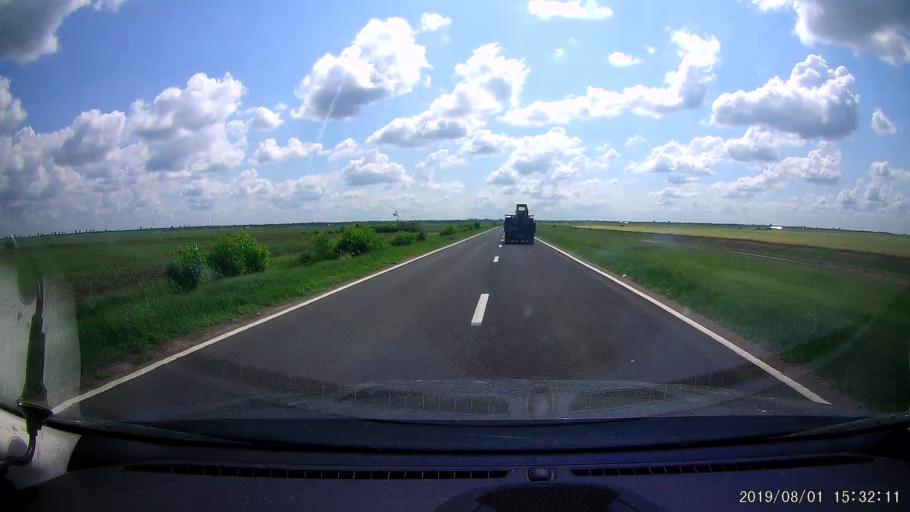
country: RO
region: Braila
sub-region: Comuna Insuratei
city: Insuratei
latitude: 44.9351
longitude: 27.6426
